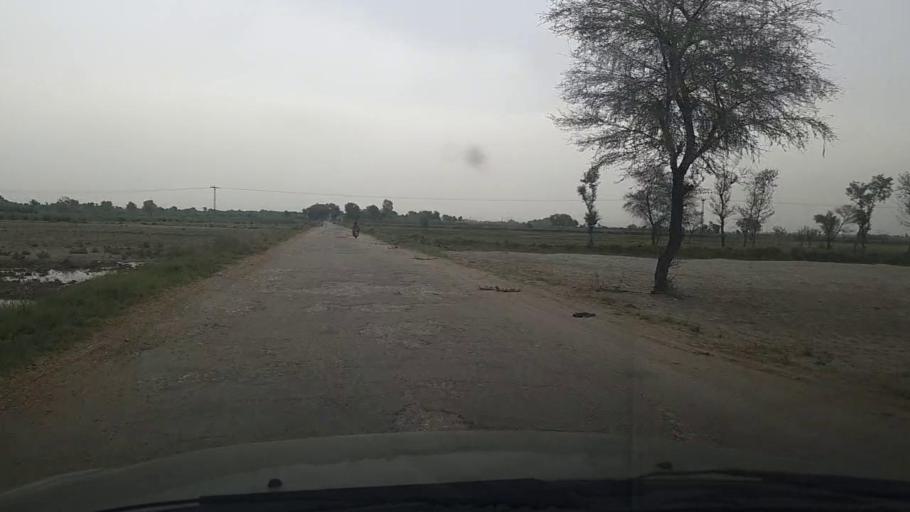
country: PK
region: Sindh
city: Daur
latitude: 26.3895
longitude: 68.1943
